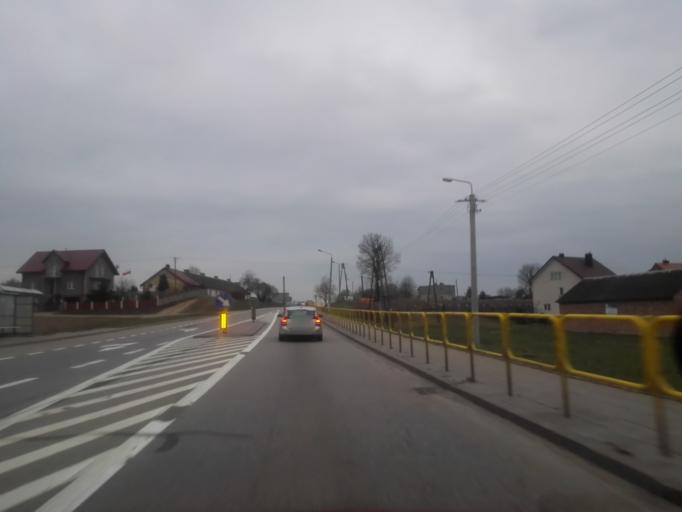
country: PL
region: Podlasie
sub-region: Powiat lomzynski
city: Piatnica
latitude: 53.2538
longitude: 22.1212
